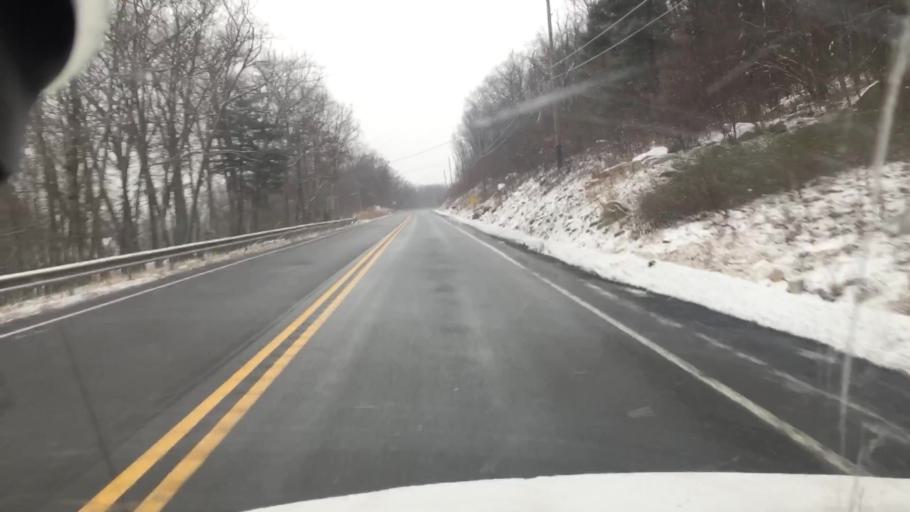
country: US
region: Pennsylvania
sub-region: Luzerne County
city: Conyngham
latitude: 41.0309
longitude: -76.0948
